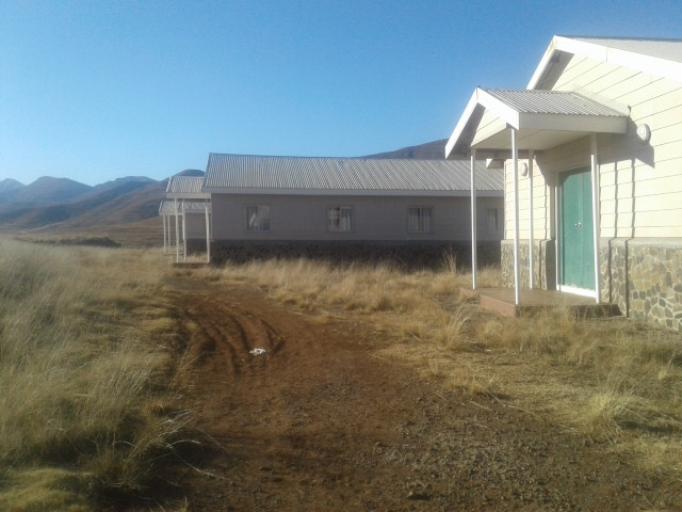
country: LS
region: Berea
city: Teyateyaneng
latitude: -29.3714
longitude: 28.0362
